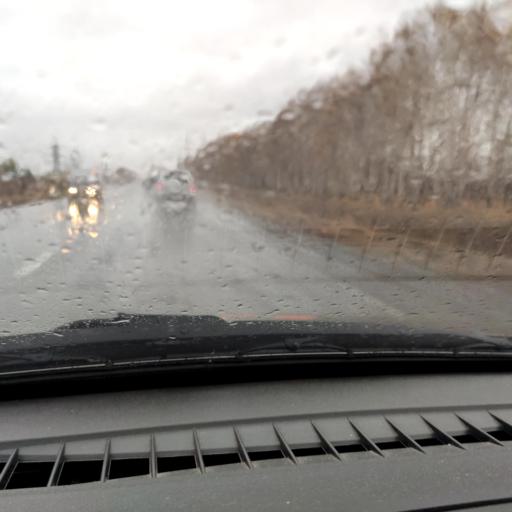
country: RU
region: Samara
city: Tol'yatti
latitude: 53.5832
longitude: 49.3341
